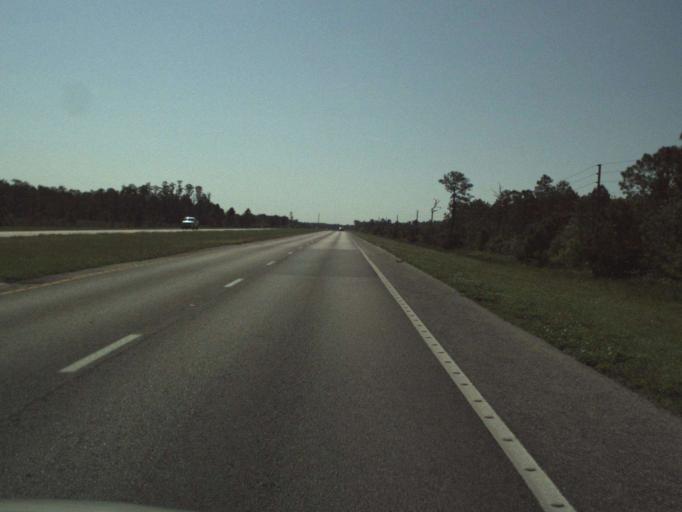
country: US
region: Florida
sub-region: Orange County
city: Wedgefield
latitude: 28.4750
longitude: -81.0178
